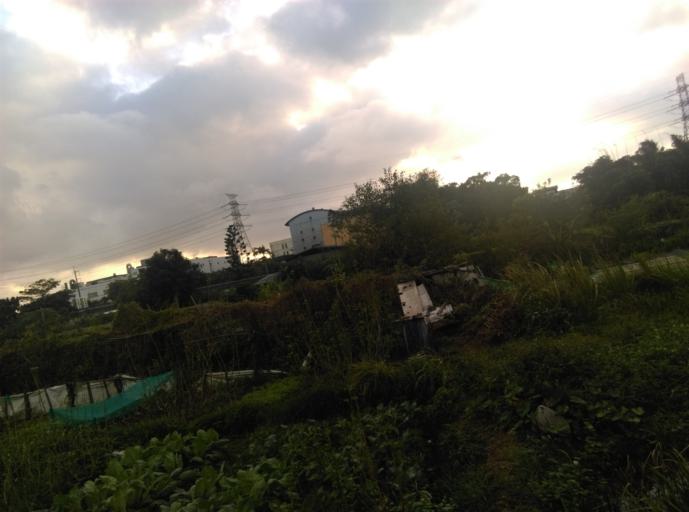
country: TW
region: Taiwan
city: Taoyuan City
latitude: 24.9944
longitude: 121.2514
